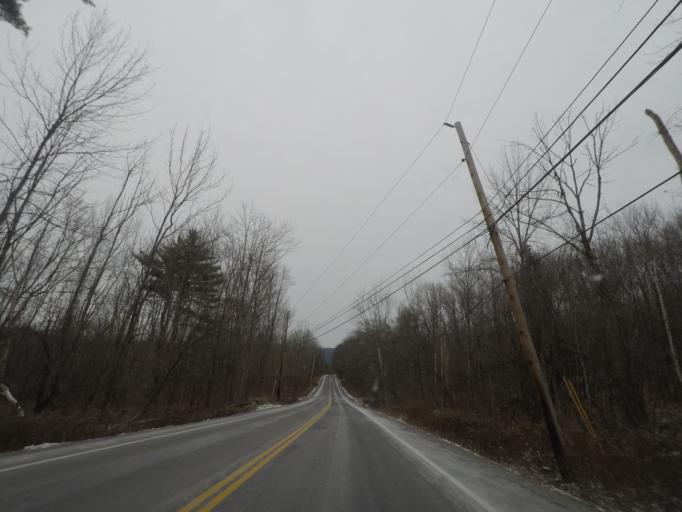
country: US
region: New York
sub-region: Rensselaer County
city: Hoosick Falls
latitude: 42.7598
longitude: -73.3754
